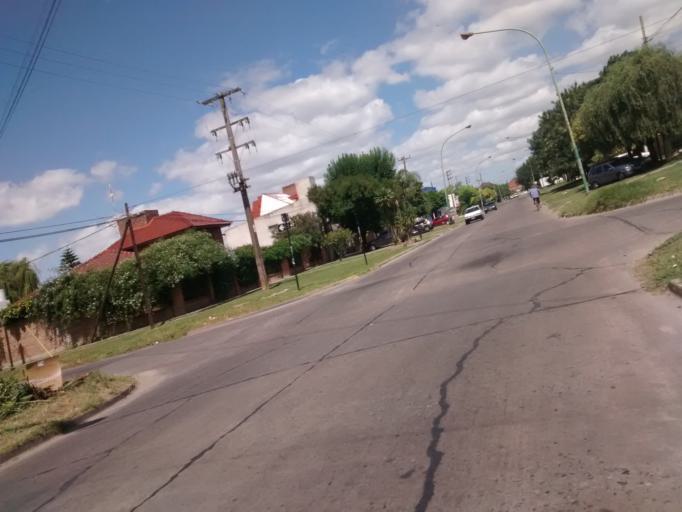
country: AR
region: Buenos Aires
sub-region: Partido de La Plata
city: La Plata
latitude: -34.9414
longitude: -57.9837
